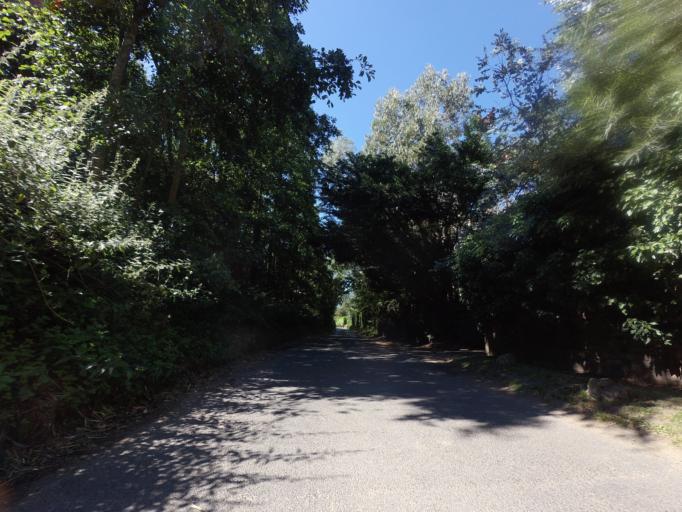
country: GB
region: England
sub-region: Kent
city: Ash
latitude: 51.2854
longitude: 1.2480
